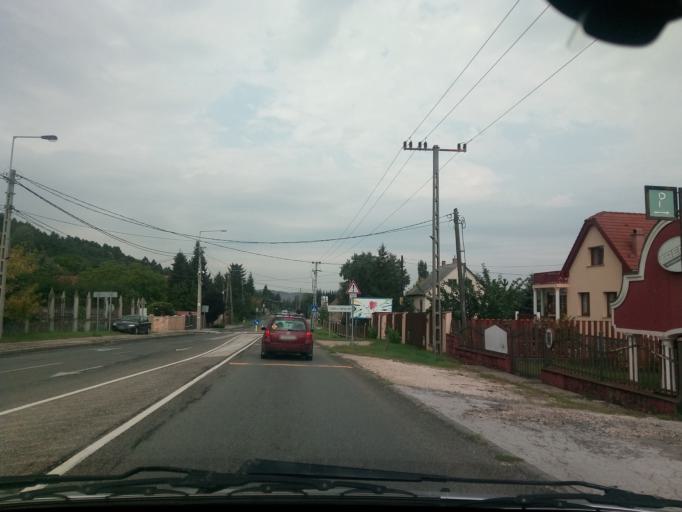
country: HU
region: Pest
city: Piliscsaba
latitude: 47.6307
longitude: 18.8430
